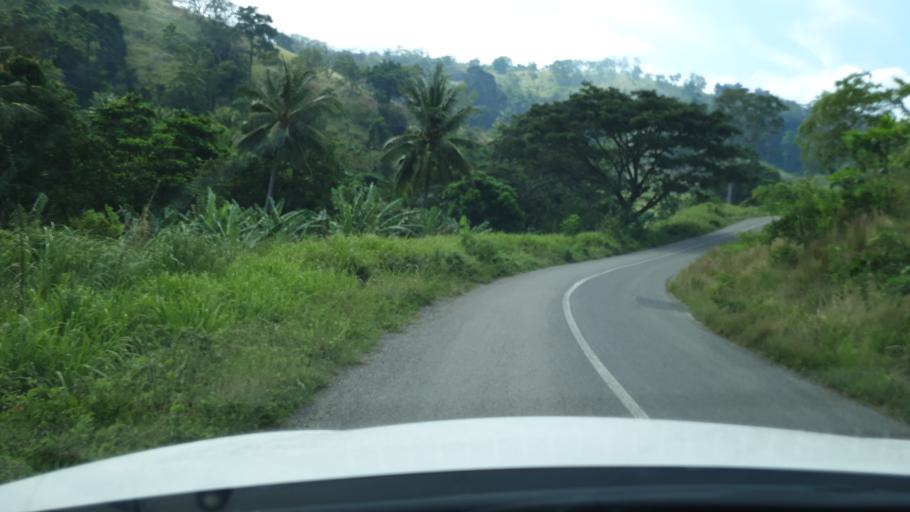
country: PG
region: Central Province
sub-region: Rigo
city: Kwikila
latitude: -9.8313
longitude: 147.5626
